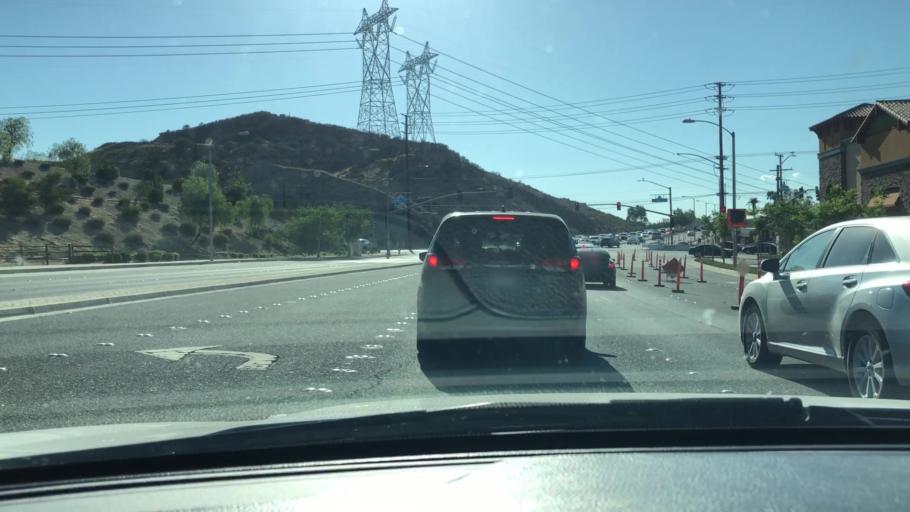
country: US
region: California
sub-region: Los Angeles County
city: Santa Clarita
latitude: 34.3952
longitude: -118.4838
